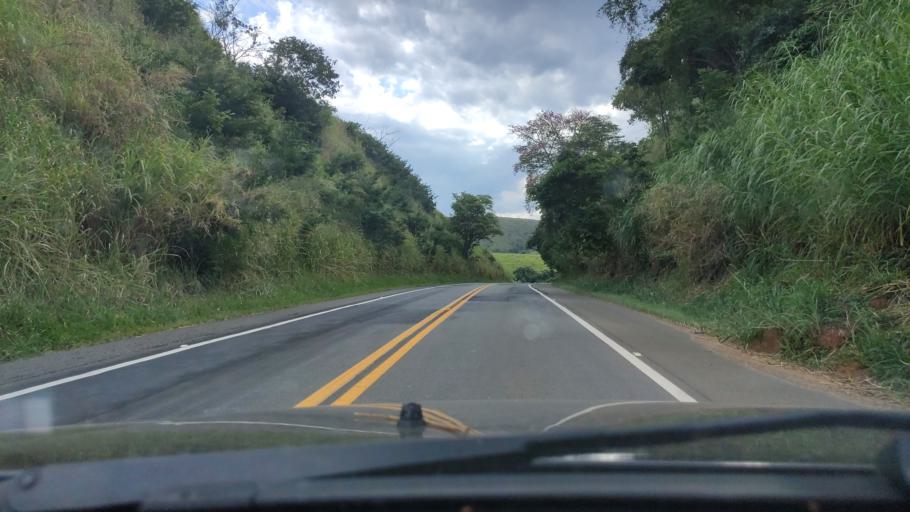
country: BR
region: Sao Paulo
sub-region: Itapira
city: Itapira
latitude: -22.4598
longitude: -46.7391
